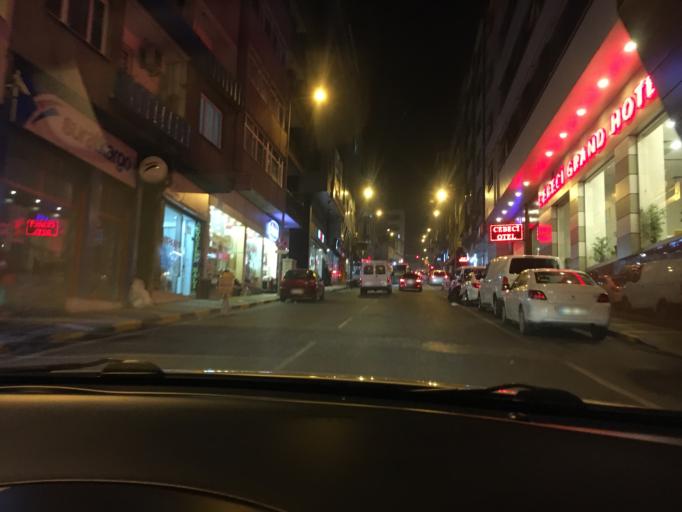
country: TR
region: Trabzon
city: Trabzon
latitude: 41.0080
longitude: 39.7260
